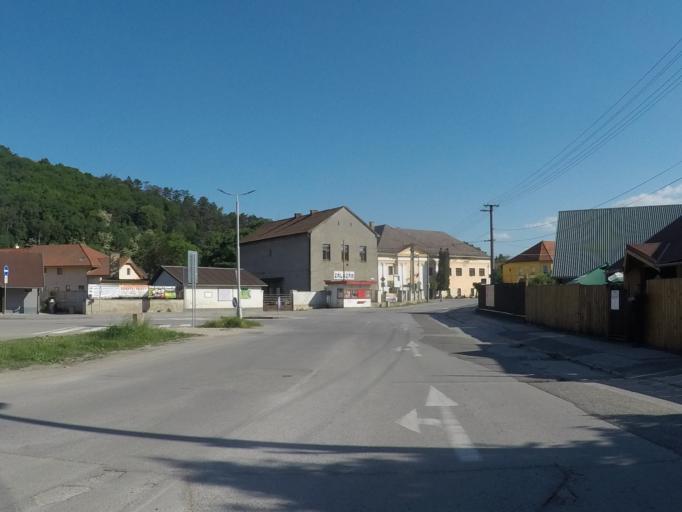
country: SK
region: Kosicky
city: Roznava
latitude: 48.5487
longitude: 20.4051
